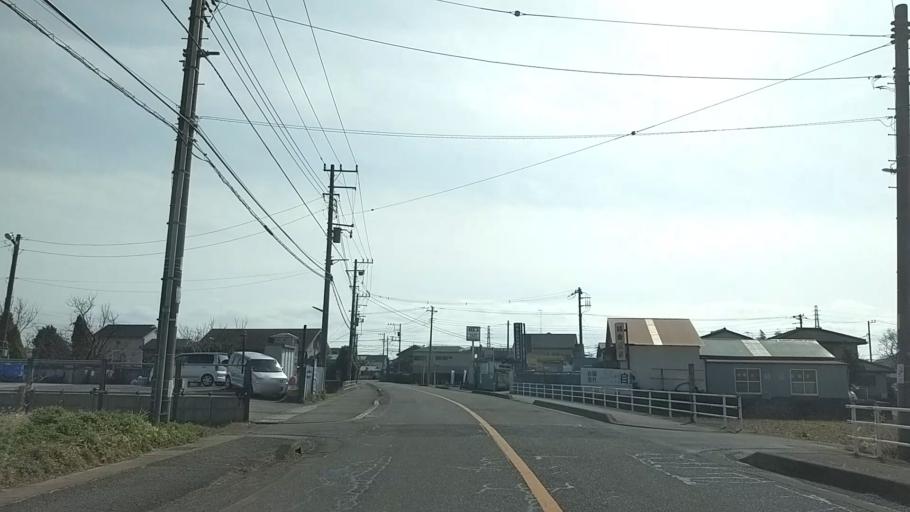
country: JP
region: Kanagawa
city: Chigasaki
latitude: 35.3569
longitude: 139.3843
